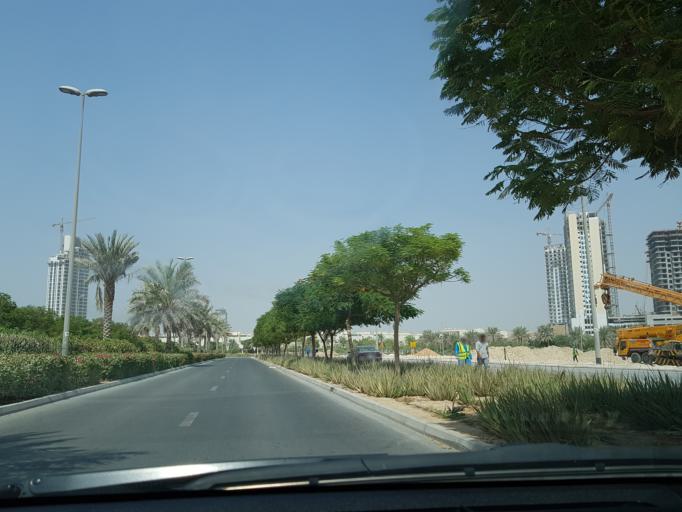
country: AE
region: Dubai
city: Dubai
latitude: 25.0542
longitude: 55.2110
